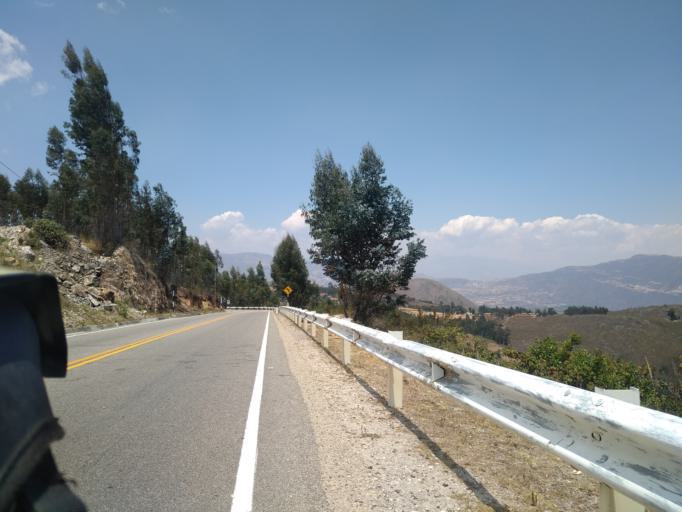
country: PE
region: Cajamarca
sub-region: San Marcos
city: San Marcos
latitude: -7.2854
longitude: -78.2145
